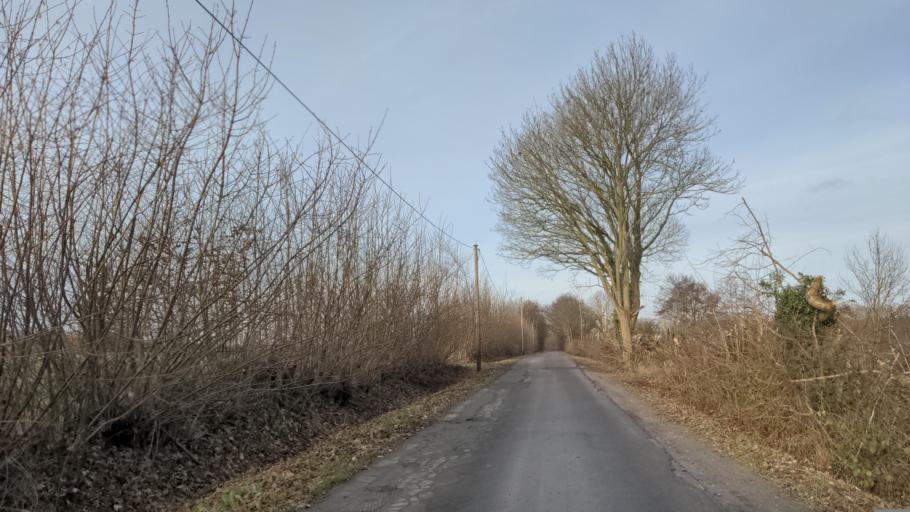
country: DE
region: Schleswig-Holstein
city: Eutin
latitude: 54.1648
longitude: 10.6280
